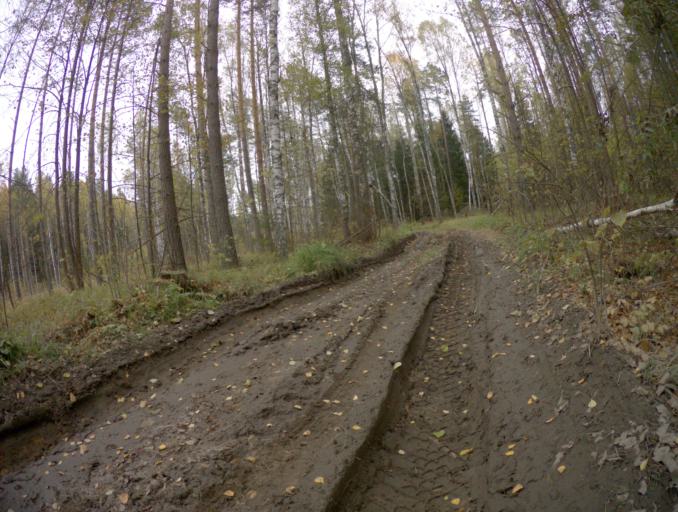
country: RU
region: Vladimir
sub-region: Kovrovskiy Rayon
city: Kovrov
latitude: 56.3145
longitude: 41.5319
